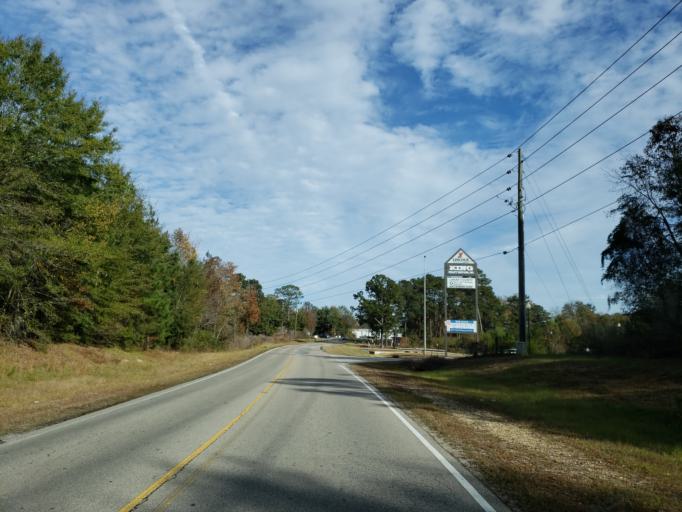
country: US
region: Mississippi
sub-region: Lamar County
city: West Hattiesburg
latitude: 31.3109
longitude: -89.4016
